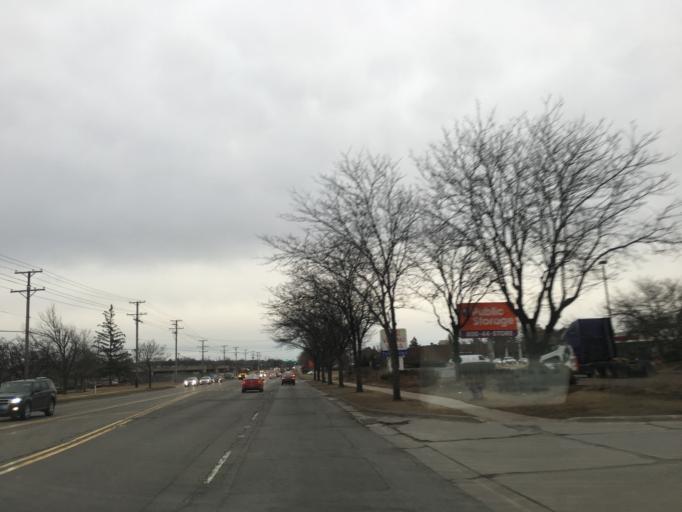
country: US
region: Illinois
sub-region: Cook County
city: Hoffman Estates
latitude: 42.0742
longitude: -88.0624
